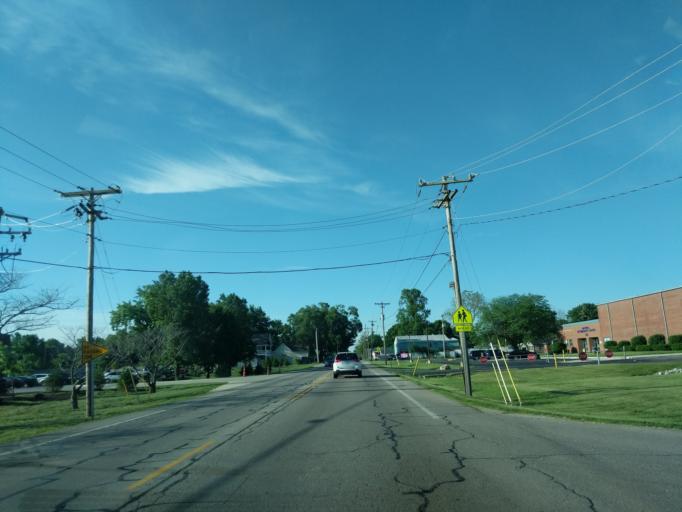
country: US
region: Indiana
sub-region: Hancock County
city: Greenfield
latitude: 39.8599
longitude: -85.7700
